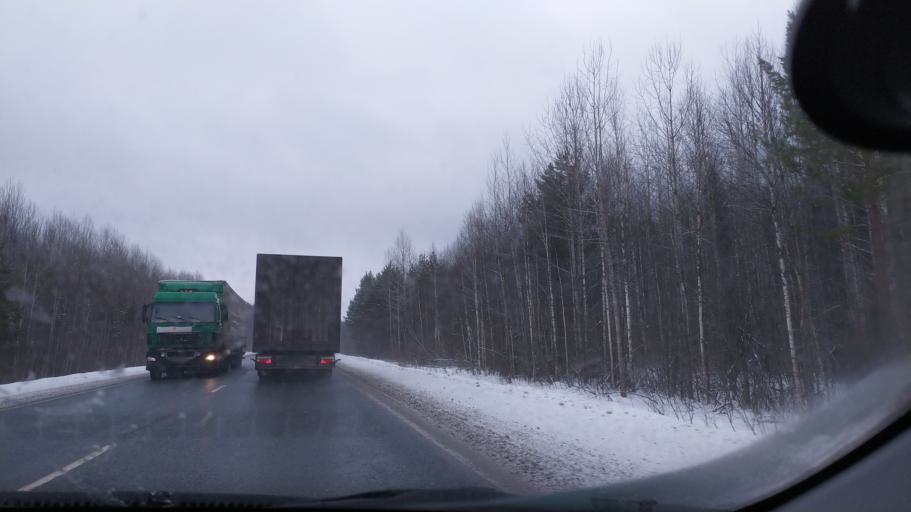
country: RU
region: Chuvashia
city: Mariinskiy Posad
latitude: 56.1876
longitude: 47.8283
